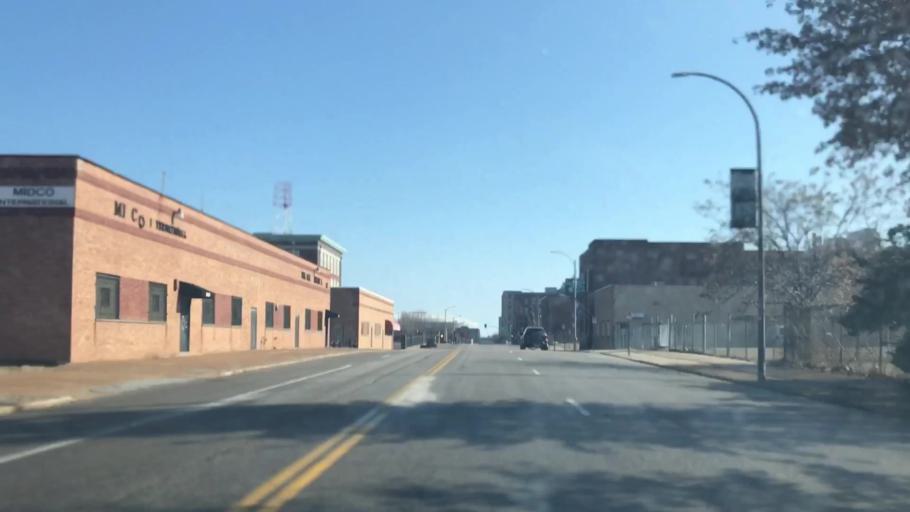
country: US
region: Missouri
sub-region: City of Saint Louis
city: St. Louis
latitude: 38.6355
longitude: -90.2071
